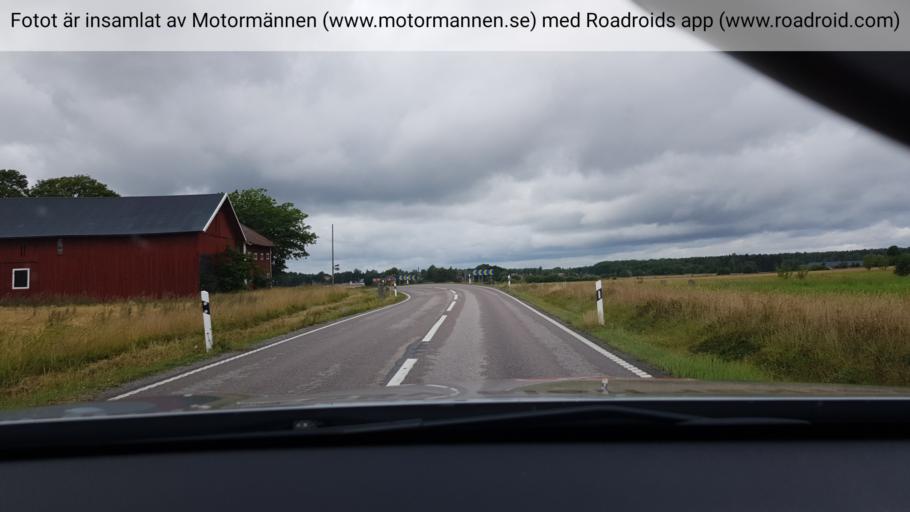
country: SE
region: Stockholm
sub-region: Norrtalje Kommun
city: Rimbo
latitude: 59.7419
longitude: 18.3953
